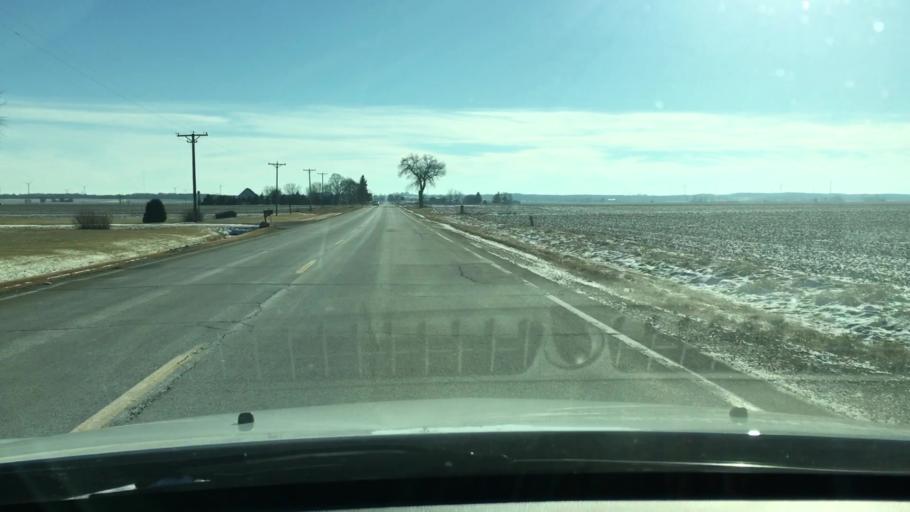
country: US
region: Illinois
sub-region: Ogle County
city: Rochelle
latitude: 41.7679
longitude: -89.0837
